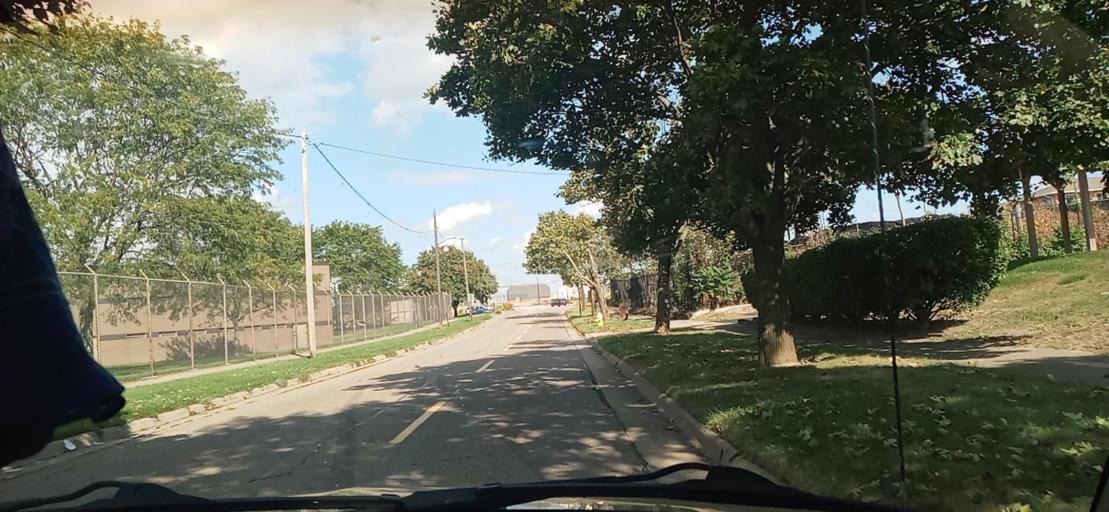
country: US
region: Ohio
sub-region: Summit County
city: Akron
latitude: 41.0597
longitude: -81.5192
